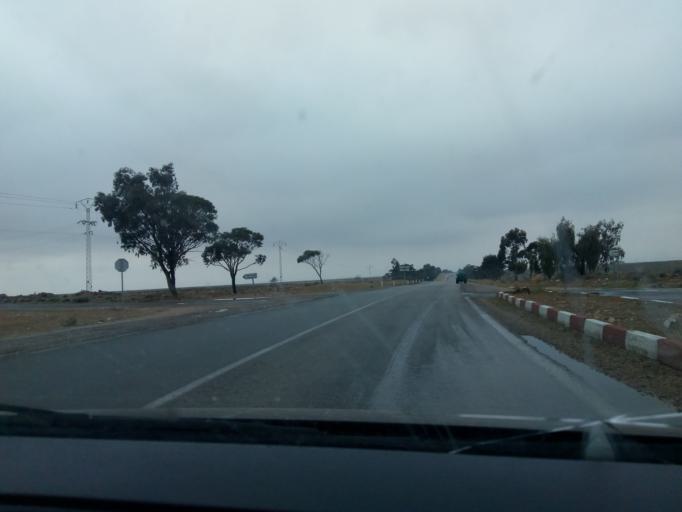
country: TN
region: Madanin
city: Medenine
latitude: 33.2718
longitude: 10.4681
